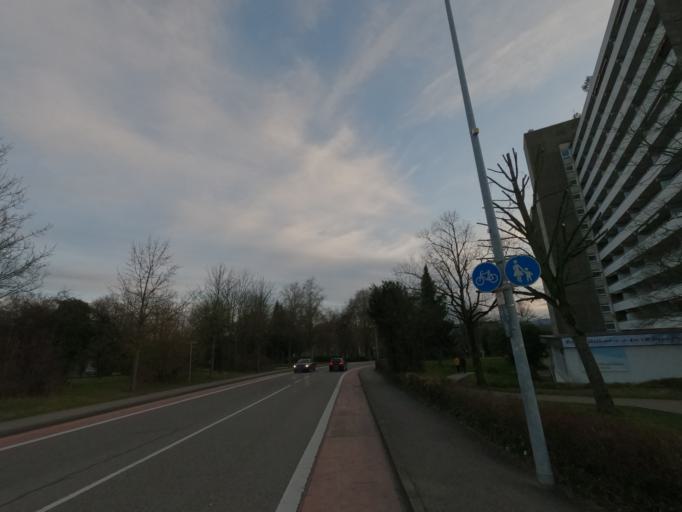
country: DE
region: Baden-Wuerttemberg
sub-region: Regierungsbezirk Stuttgart
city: Goeppingen
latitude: 48.7080
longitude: 9.6742
